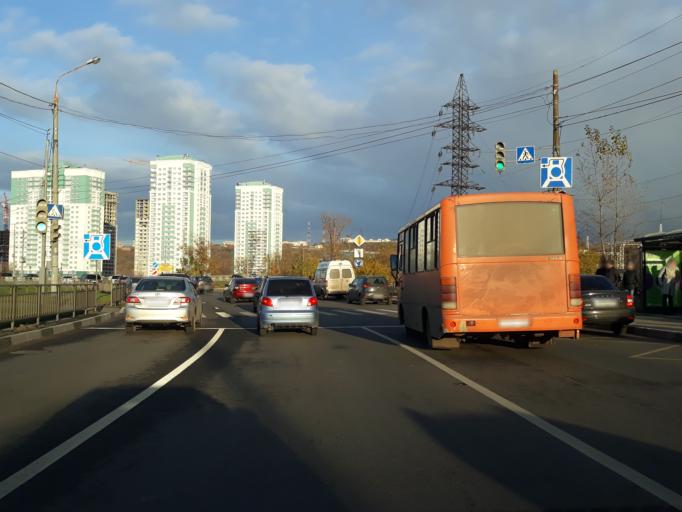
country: RU
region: Nizjnij Novgorod
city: Nizhniy Novgorod
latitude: 56.2979
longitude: 43.9455
